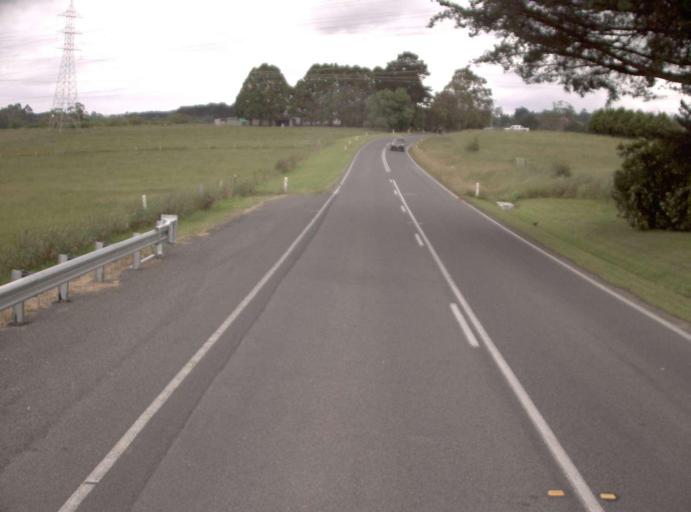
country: AU
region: Victoria
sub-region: Baw Baw
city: Warragul
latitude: -38.1166
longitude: 145.9788
